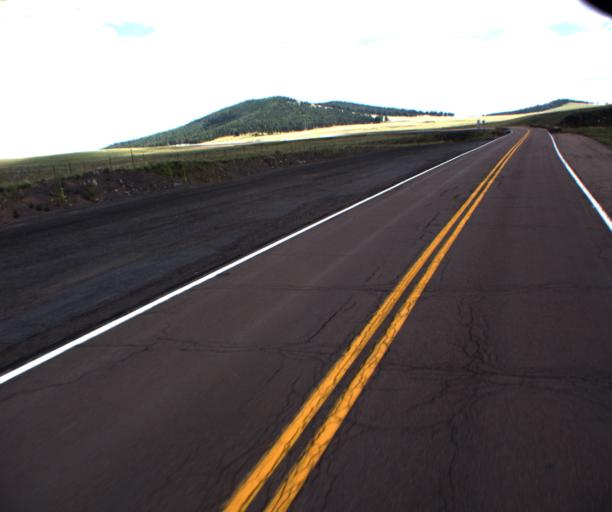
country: US
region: Arizona
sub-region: Apache County
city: Eagar
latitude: 34.0529
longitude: -109.5456
